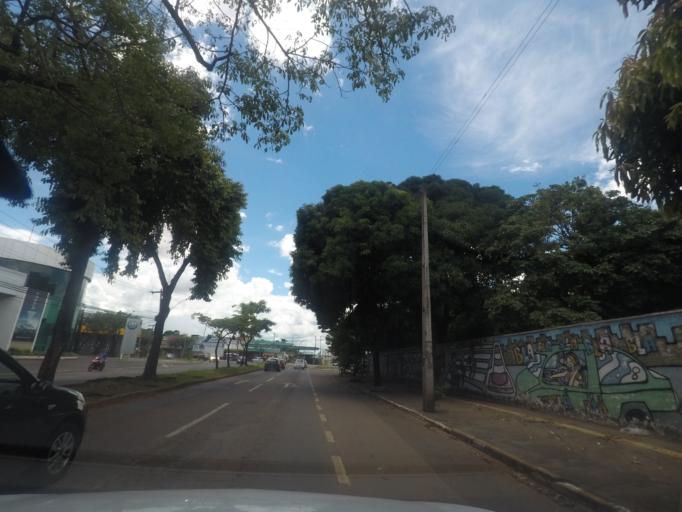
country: BR
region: Goias
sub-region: Goiania
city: Goiania
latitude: -16.6811
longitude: -49.3089
